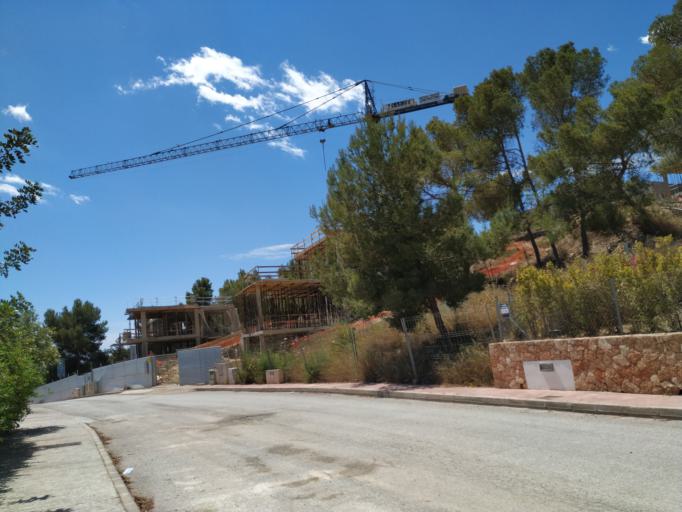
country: ES
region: Balearic Islands
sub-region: Illes Balears
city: Ibiza
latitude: 38.9194
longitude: 1.4726
